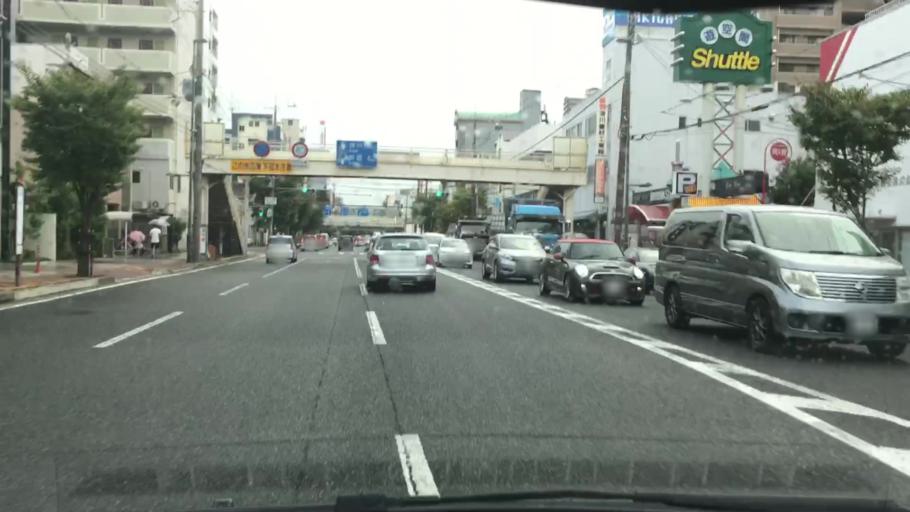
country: JP
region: Hyogo
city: Nishinomiya-hama
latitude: 34.7410
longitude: 135.3393
